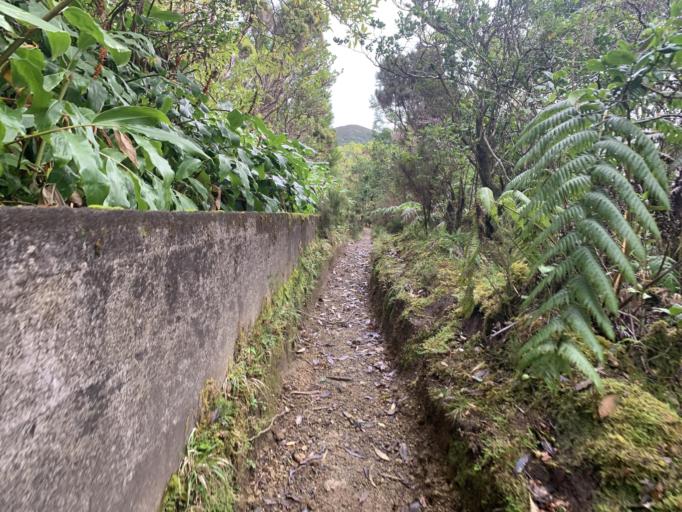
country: PT
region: Azores
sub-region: Vila Franca do Campo
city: Vila Franca do Campo
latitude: 37.7485
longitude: -25.4750
